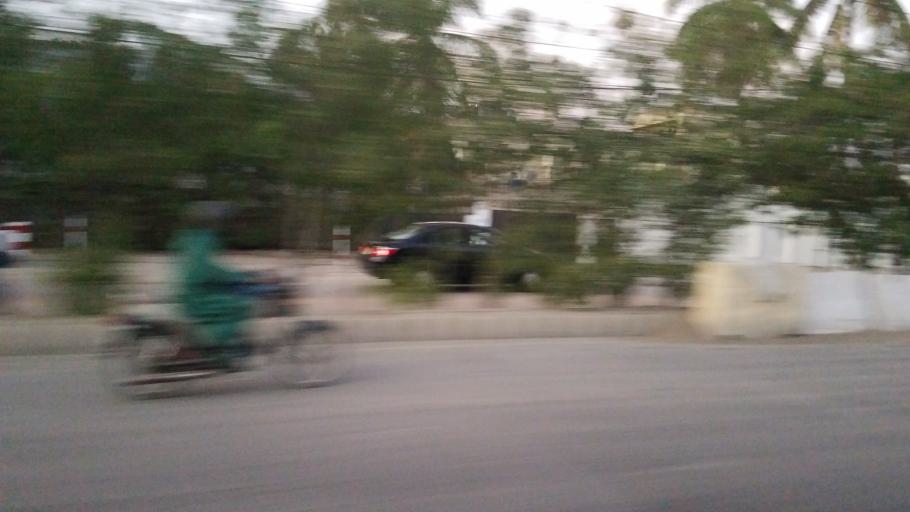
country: PK
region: Sindh
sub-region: Karachi District
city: Karachi
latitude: 24.8276
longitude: 67.0315
